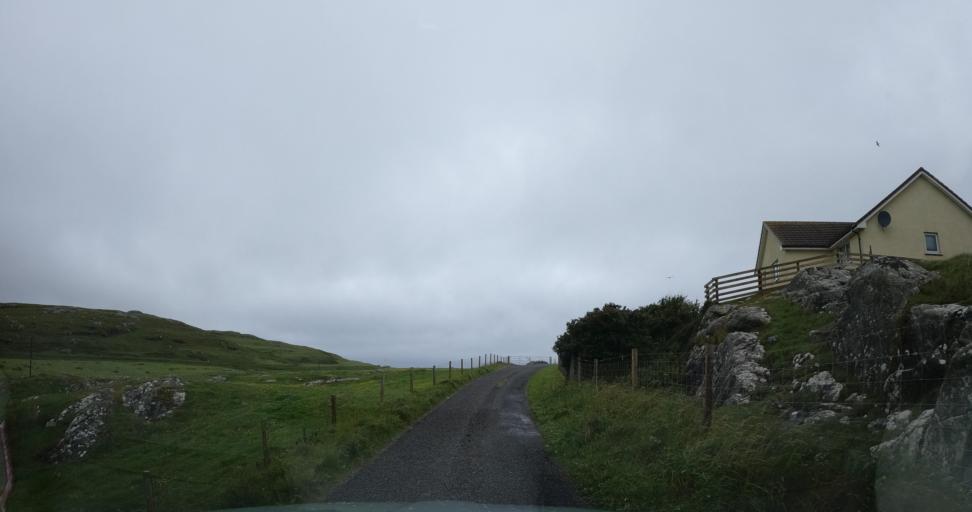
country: GB
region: Scotland
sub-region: Eilean Siar
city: Barra
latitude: 57.0046
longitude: -7.4922
